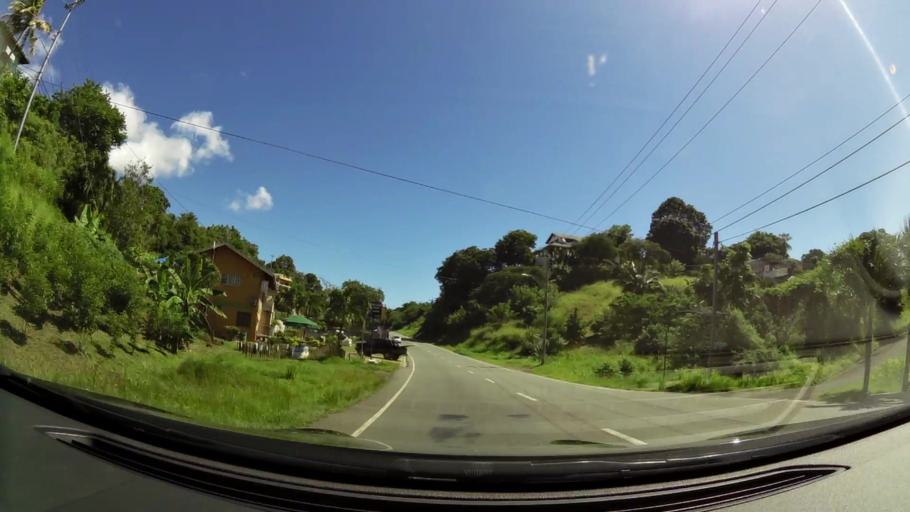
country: TT
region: Tobago
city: Scarborough
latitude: 11.1794
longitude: -60.7970
